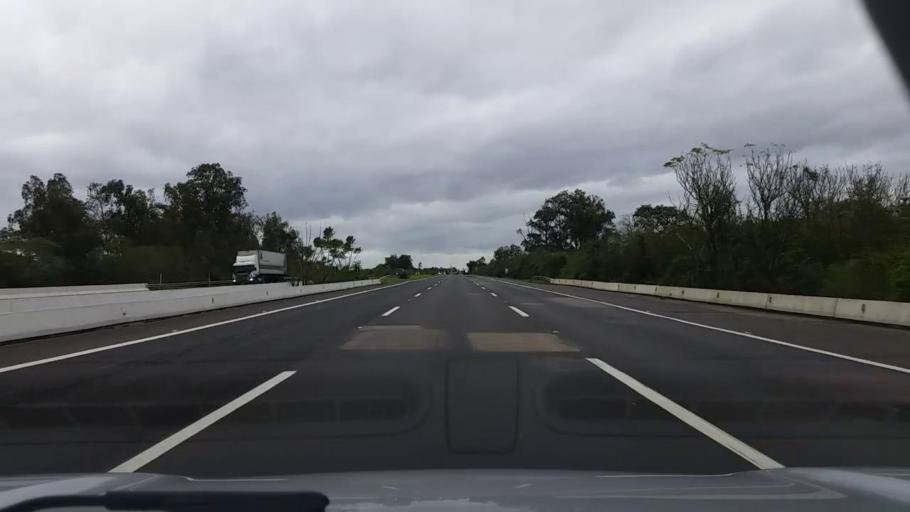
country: BR
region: Rio Grande do Sul
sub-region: Rolante
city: Rolante
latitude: -29.8835
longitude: -50.5500
